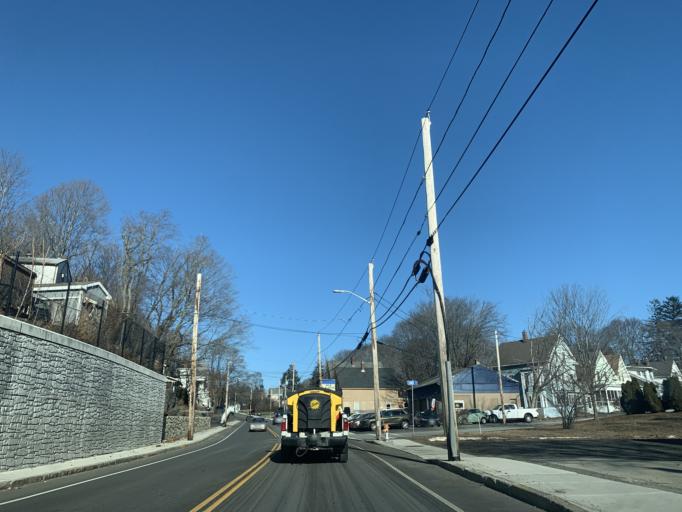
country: US
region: Massachusetts
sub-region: Middlesex County
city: Marlborough
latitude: 42.3478
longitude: -71.5426
